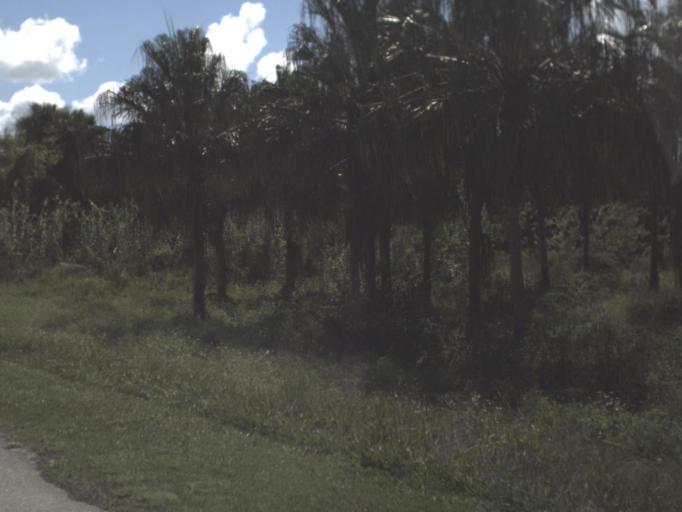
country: US
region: Florida
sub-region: Okeechobee County
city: Taylor Creek
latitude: 27.1597
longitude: -80.7099
